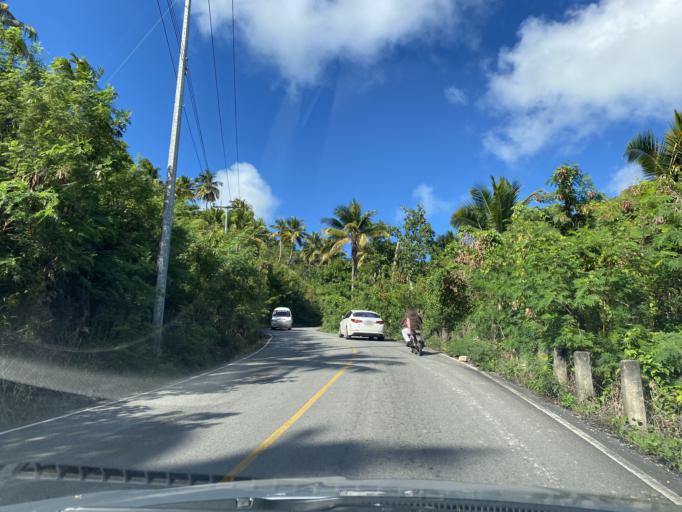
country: DO
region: Samana
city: Sanchez
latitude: 19.2365
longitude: -69.5958
